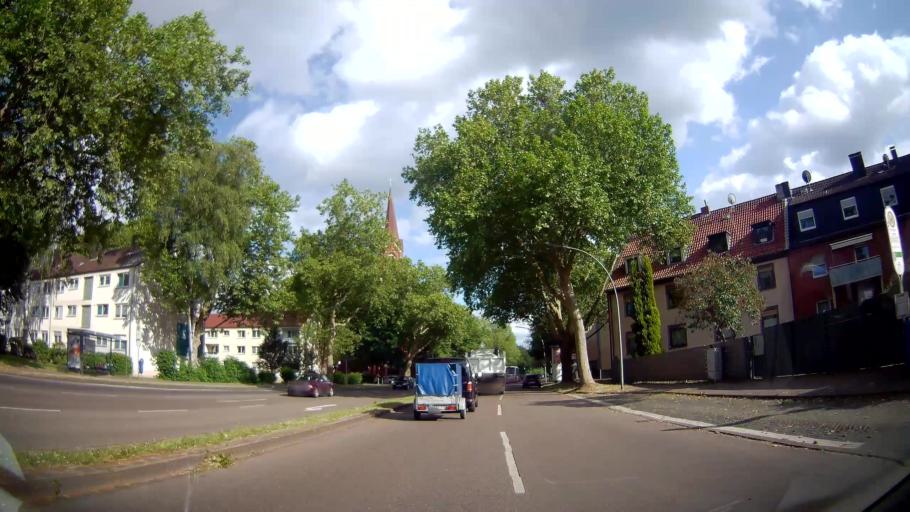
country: DE
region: North Rhine-Westphalia
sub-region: Regierungsbezirk Munster
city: Gelsenkirchen
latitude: 51.5127
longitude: 7.0716
